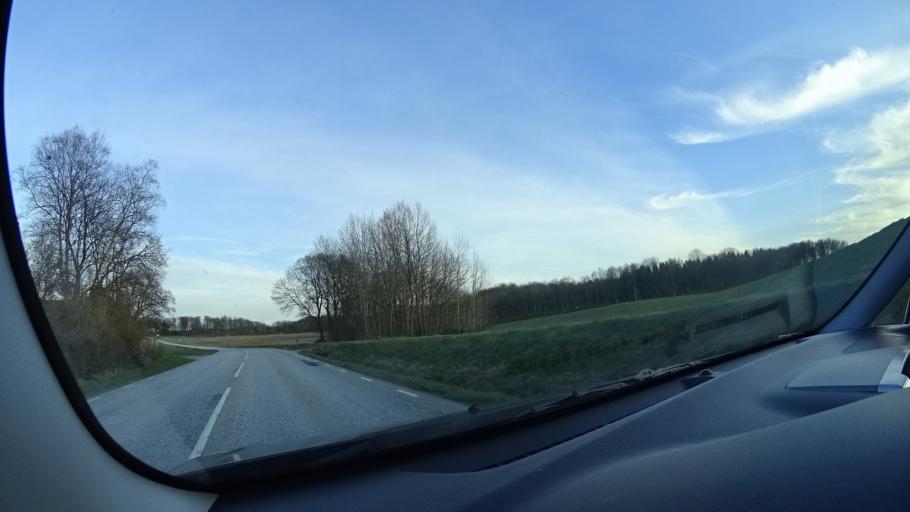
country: SE
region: Skane
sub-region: Eslovs Kommun
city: Stehag
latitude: 55.9572
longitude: 13.3382
